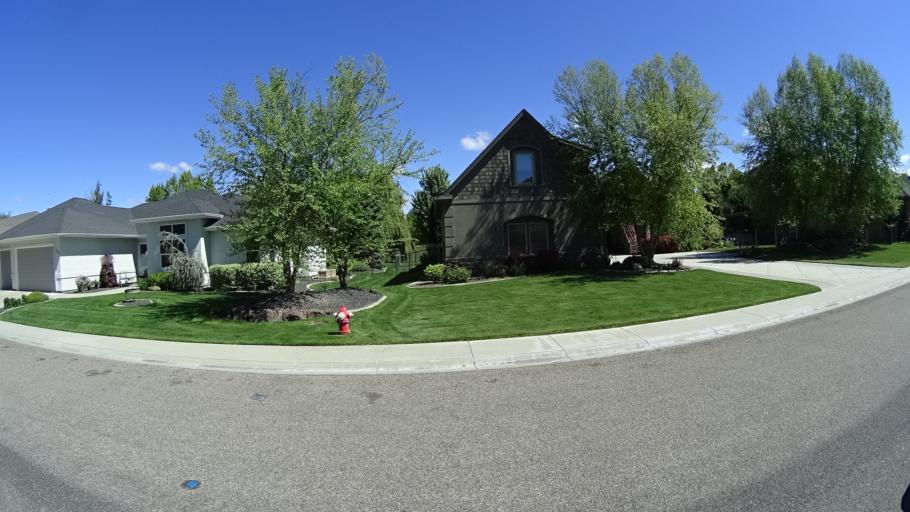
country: US
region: Idaho
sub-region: Ada County
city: Eagle
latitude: 43.6696
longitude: -116.3633
